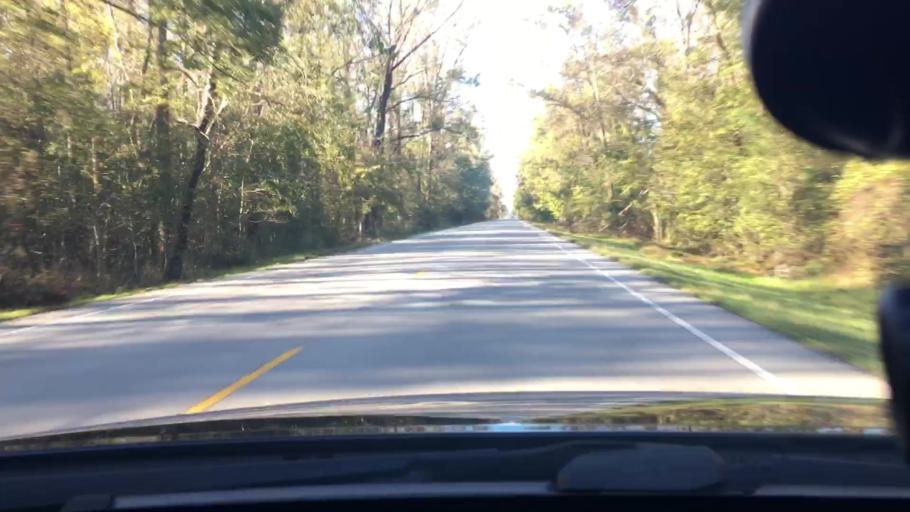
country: US
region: North Carolina
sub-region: Craven County
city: New Bern
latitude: 35.1882
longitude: -77.0510
